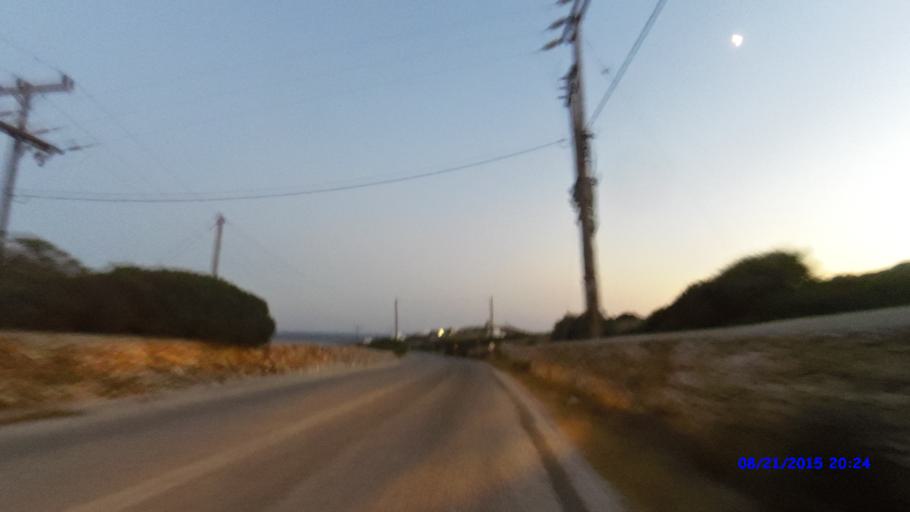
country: GR
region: South Aegean
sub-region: Nomos Kykladon
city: Antiparos
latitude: 36.9890
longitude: 25.0722
